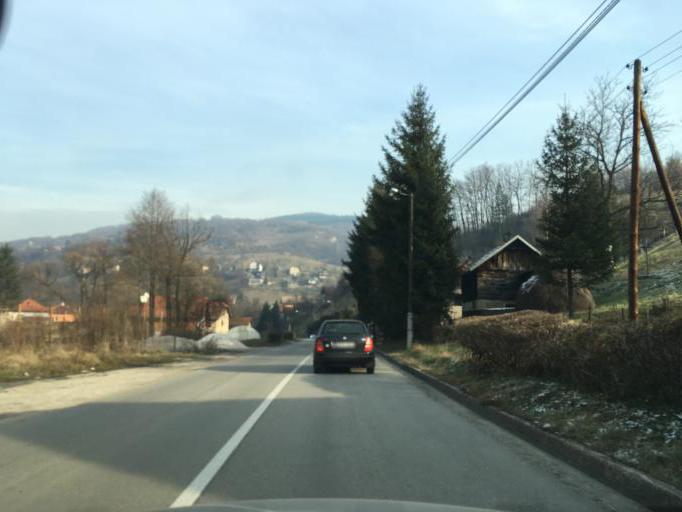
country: BA
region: Federation of Bosnia and Herzegovina
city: Lokvine
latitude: 44.1919
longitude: 17.8722
